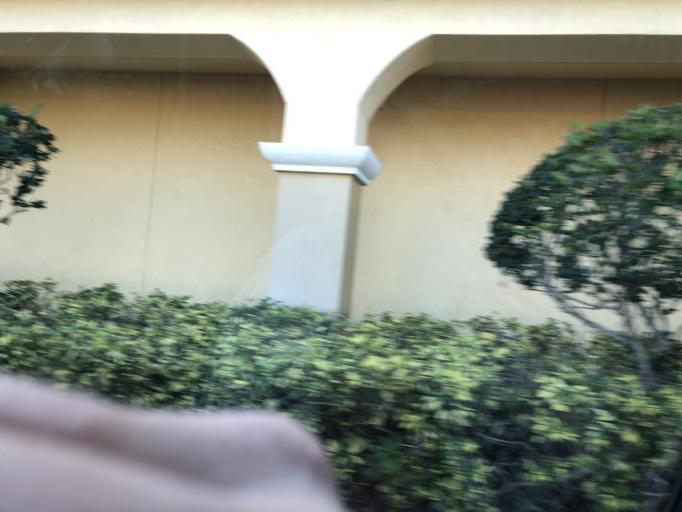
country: US
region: Florida
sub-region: Martin County
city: Stuart
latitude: 27.1917
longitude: -80.2568
